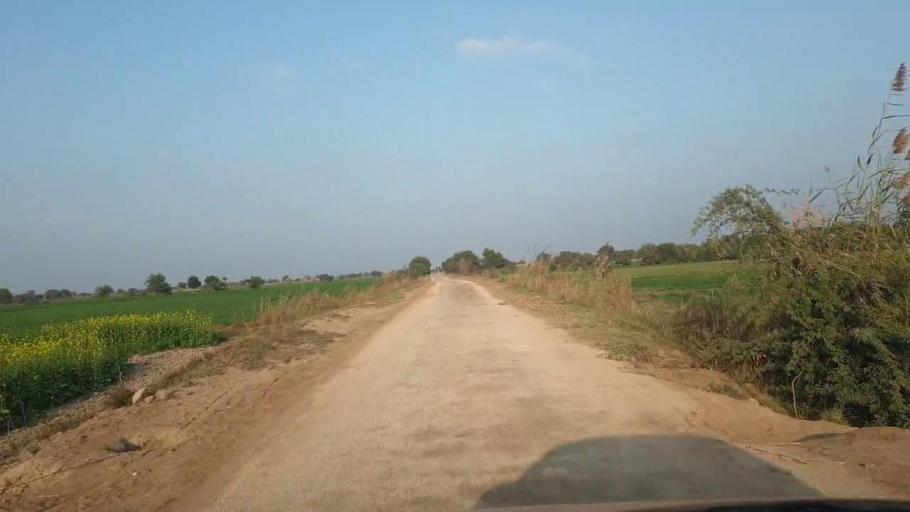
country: PK
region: Sindh
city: Berani
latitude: 25.8544
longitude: 68.7334
